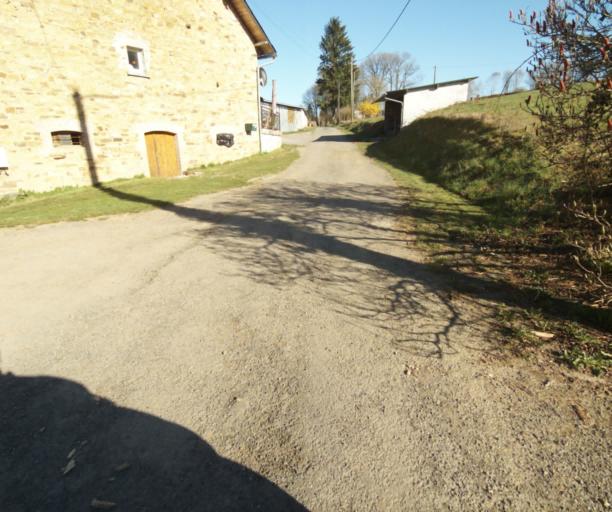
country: FR
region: Limousin
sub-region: Departement de la Correze
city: Seilhac
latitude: 45.3942
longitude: 1.7049
